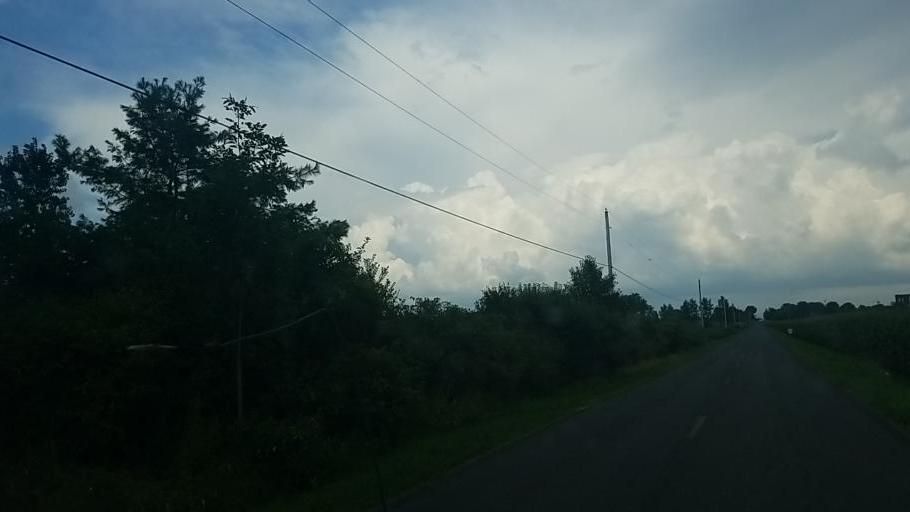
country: US
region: Ohio
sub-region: Medina County
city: Lodi
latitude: 41.0005
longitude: -82.0139
